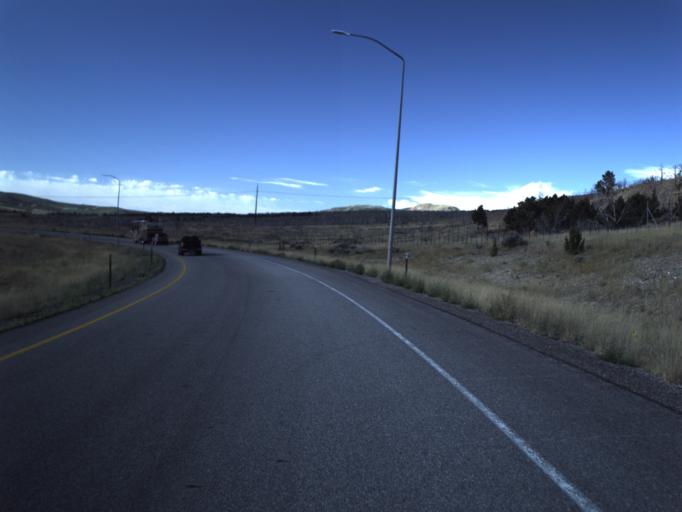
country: US
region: Utah
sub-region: Beaver County
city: Beaver
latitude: 38.5747
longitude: -112.6067
